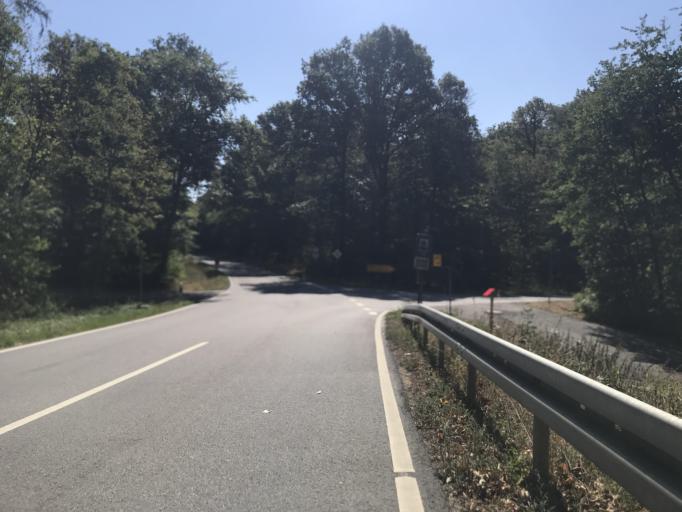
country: DE
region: Hesse
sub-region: Regierungsbezirk Darmstadt
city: Rudesheim am Rhein
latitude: 50.0473
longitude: 7.9265
